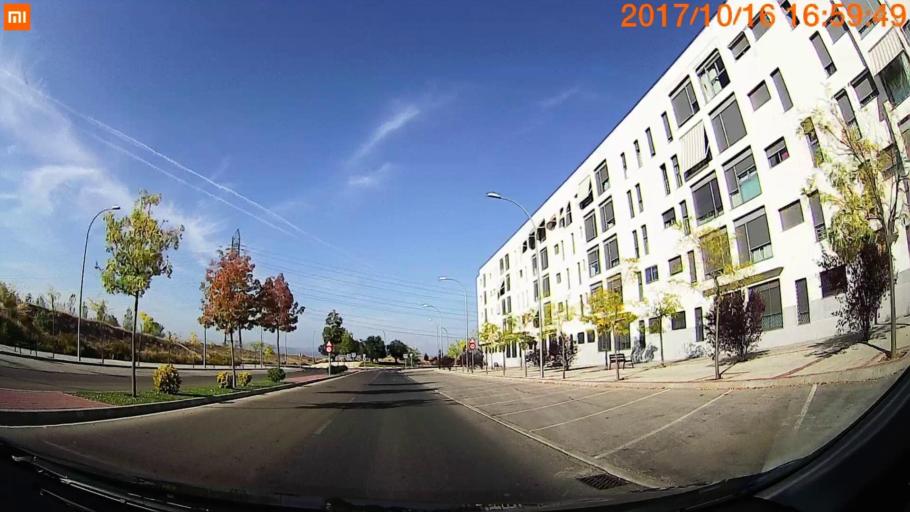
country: ES
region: Madrid
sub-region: Provincia de Madrid
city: Alcobendas
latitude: 40.5564
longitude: -3.6618
